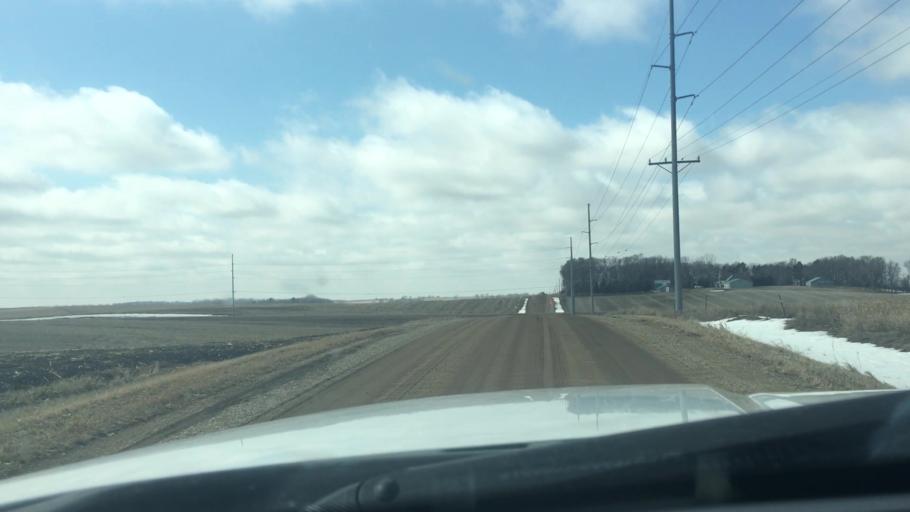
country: US
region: South Dakota
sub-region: Minnehaha County
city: Crooks
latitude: 43.6164
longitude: -96.8073
